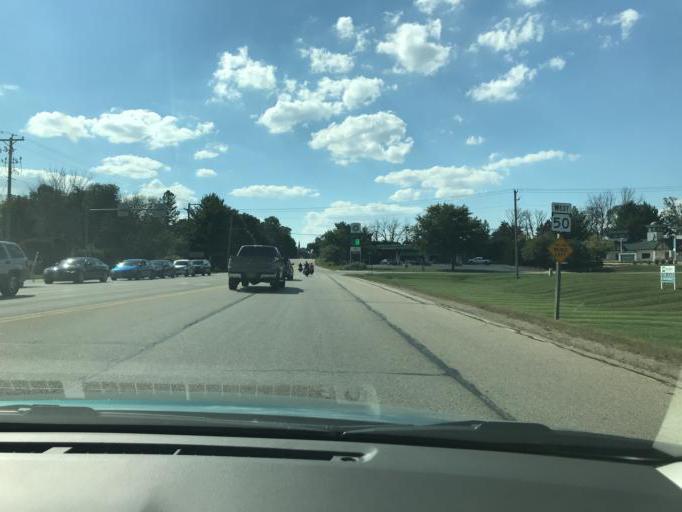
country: US
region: Wisconsin
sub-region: Walworth County
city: Lake Geneva
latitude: 42.5931
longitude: -88.4145
